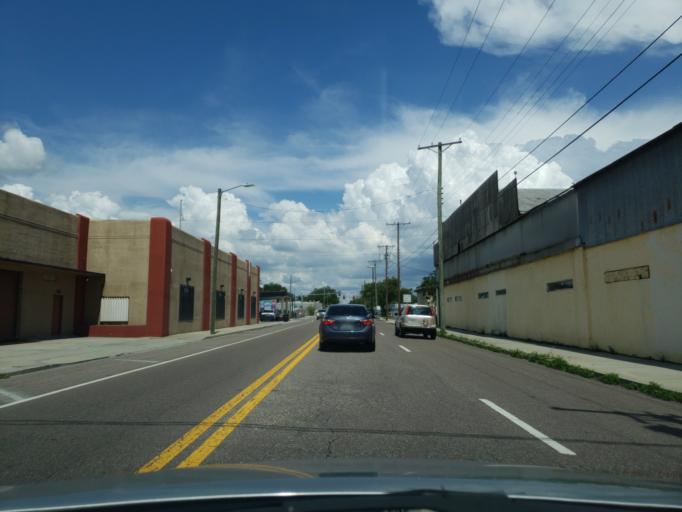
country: US
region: Florida
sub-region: Hillsborough County
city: Tampa
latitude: 27.9602
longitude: -82.4239
